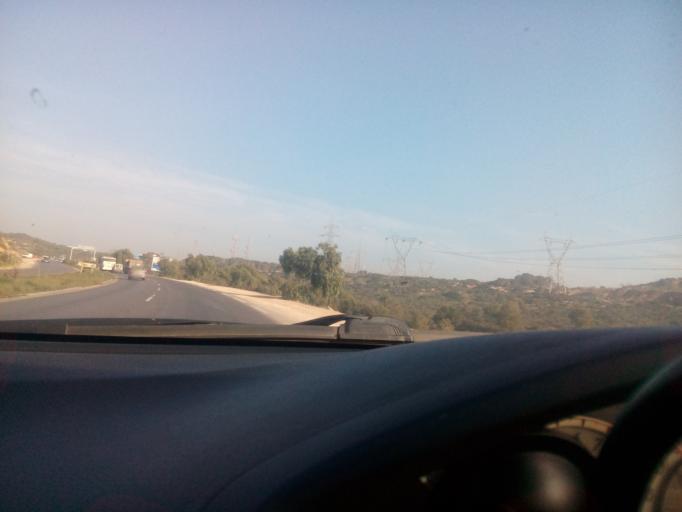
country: DZ
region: Oran
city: Oran
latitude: 35.6428
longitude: -0.7066
